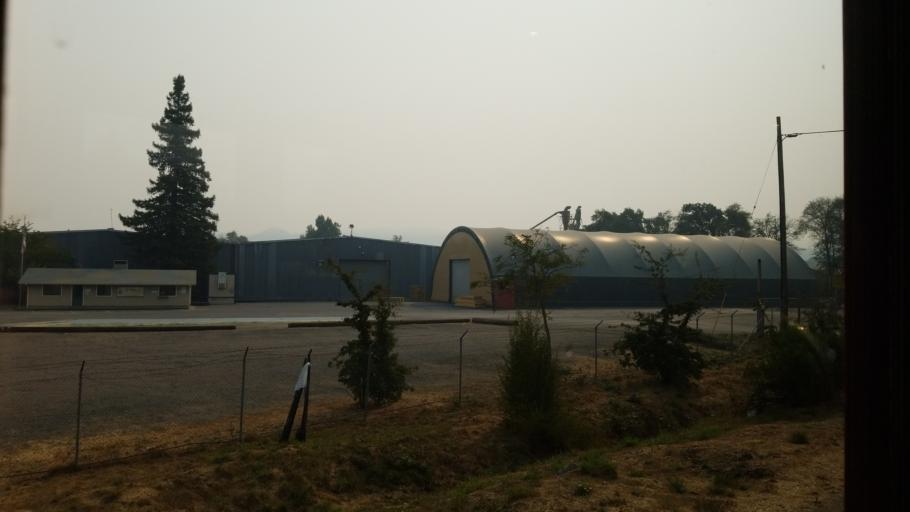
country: US
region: California
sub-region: Mendocino County
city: Willits
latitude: 39.4058
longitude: -123.3479
